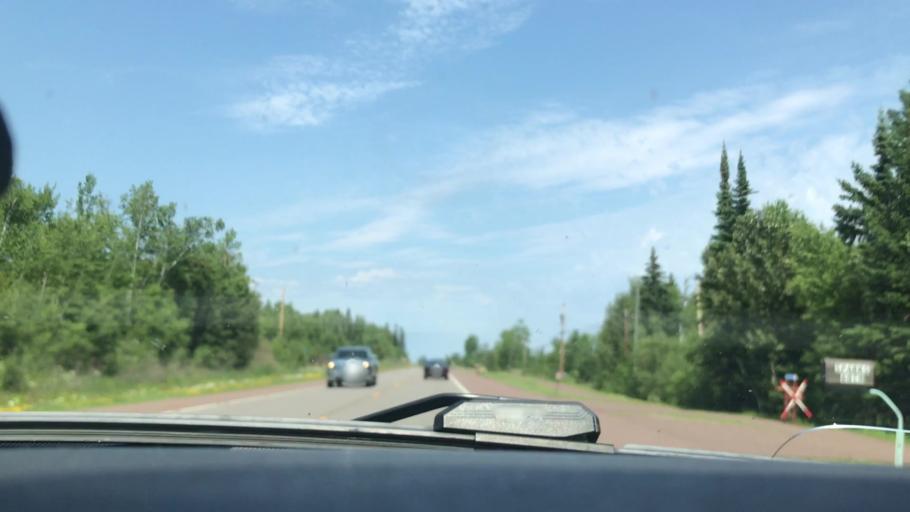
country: US
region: Minnesota
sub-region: Cook County
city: Grand Marais
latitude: 47.5909
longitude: -90.8037
